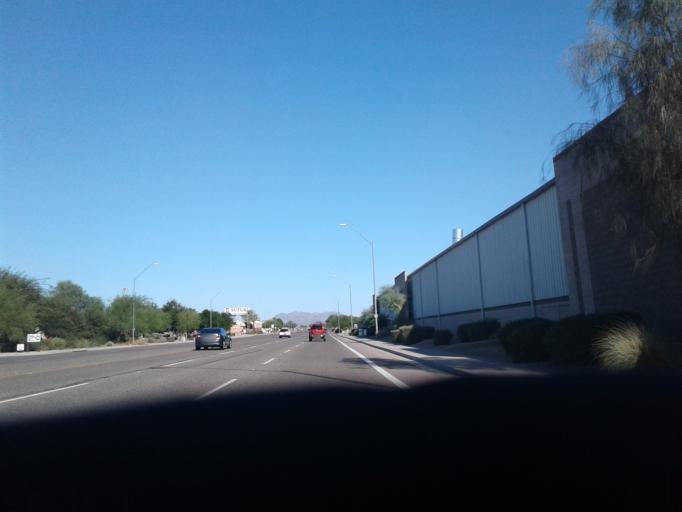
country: US
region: Arizona
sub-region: Maricopa County
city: Cave Creek
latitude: 33.6877
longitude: -112.0459
